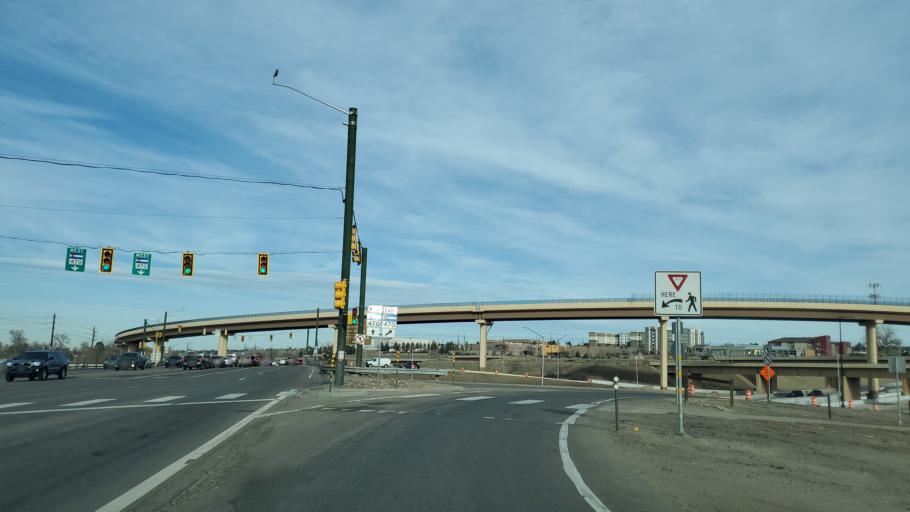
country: US
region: Colorado
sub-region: Arapahoe County
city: Columbine Valley
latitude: 39.5637
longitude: -105.0338
